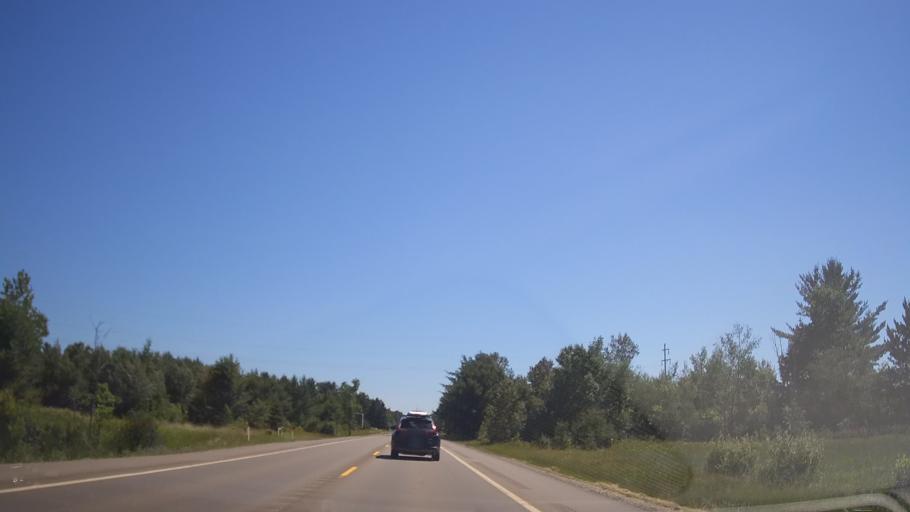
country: US
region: Michigan
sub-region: Cheboygan County
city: Indian River
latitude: 45.6014
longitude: -84.7824
